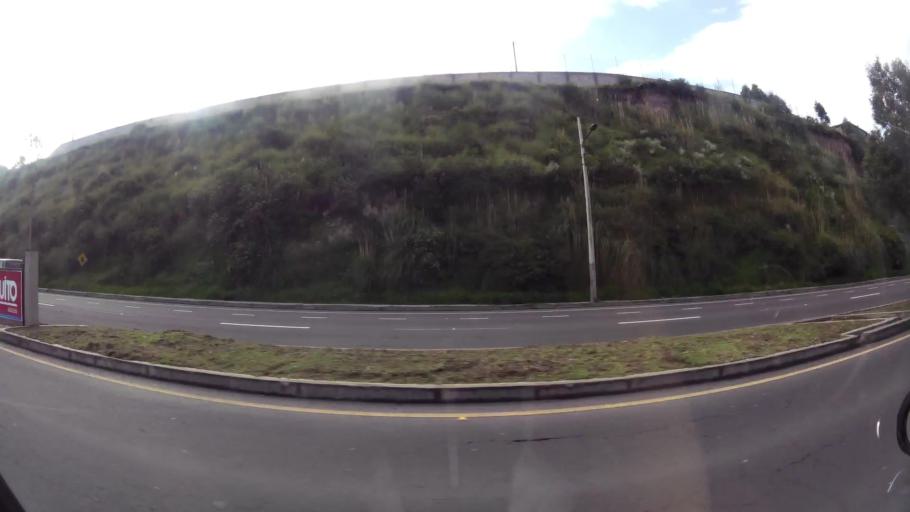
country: EC
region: Pichincha
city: Quito
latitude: -0.2389
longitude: -78.4918
